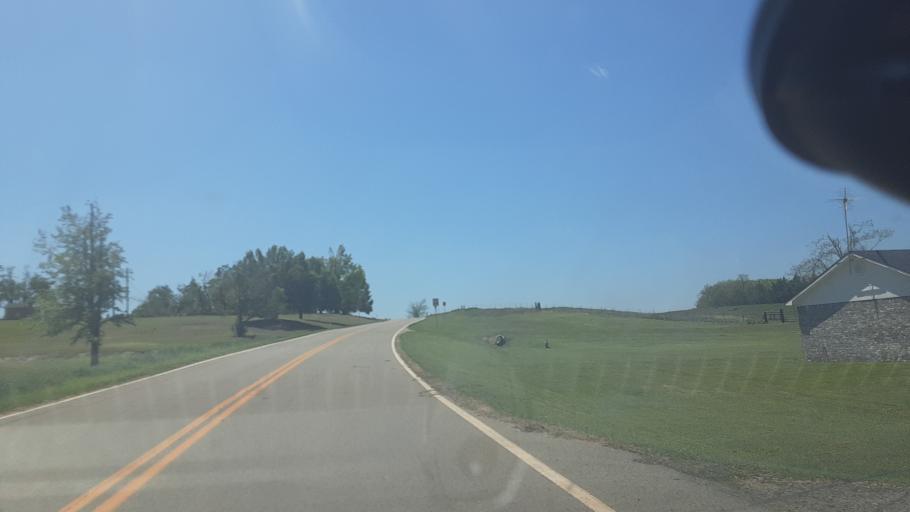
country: US
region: Oklahoma
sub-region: Logan County
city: Guthrie
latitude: 36.0620
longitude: -97.4073
